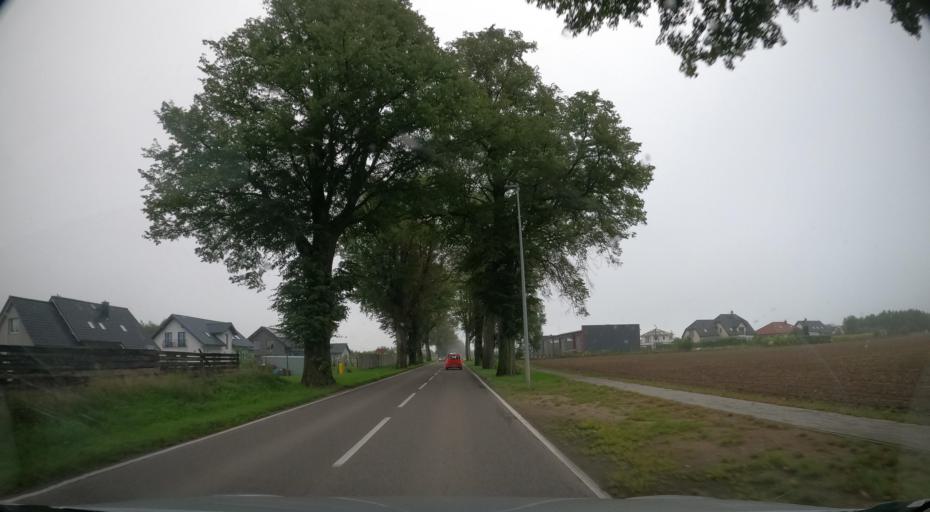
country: PL
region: Pomeranian Voivodeship
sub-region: Powiat wejherowski
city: Bojano
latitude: 54.4490
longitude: 18.3779
